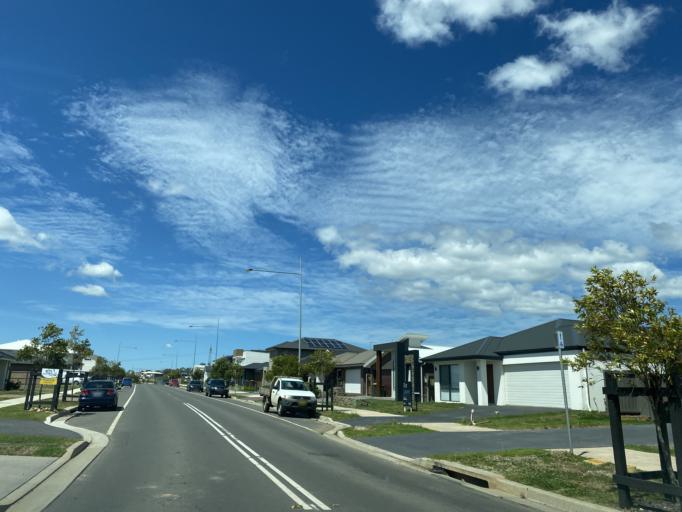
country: AU
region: New South Wales
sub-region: Camden
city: Narellan
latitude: -34.0137
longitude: 150.7802
